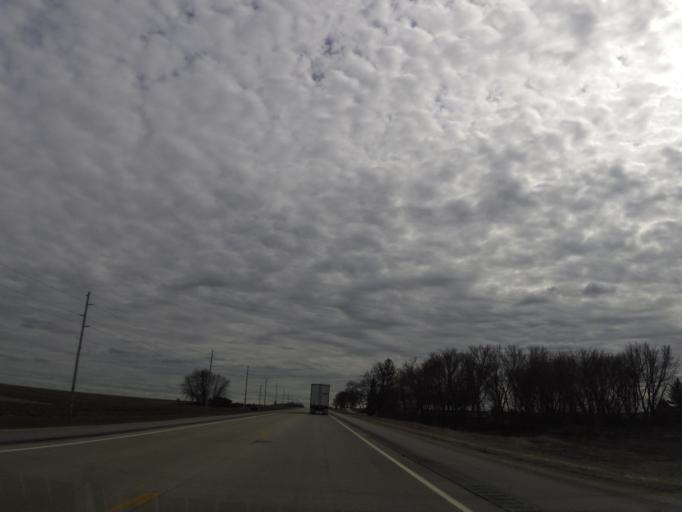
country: US
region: Minnesota
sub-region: Fillmore County
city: Spring Valley
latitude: 43.5924
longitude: -92.3893
